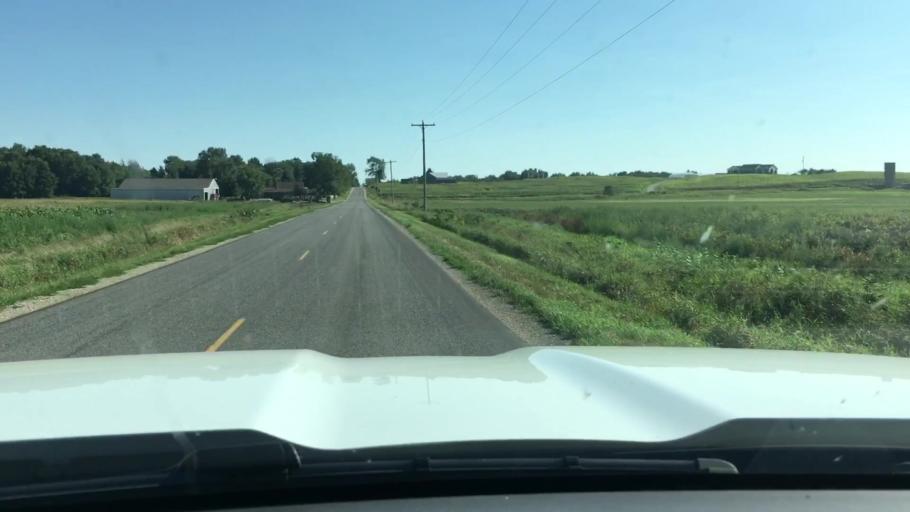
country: US
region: Michigan
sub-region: Muskegon County
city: Ravenna
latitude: 43.2683
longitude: -85.9180
